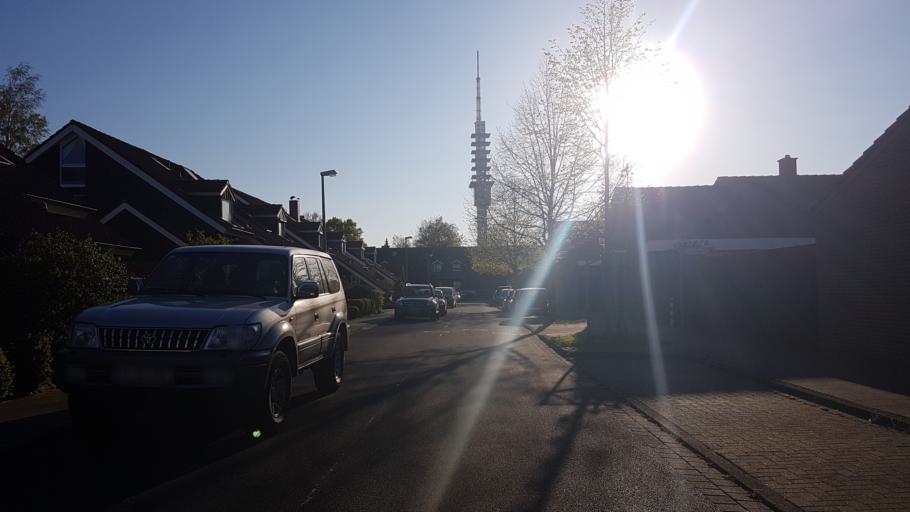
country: DE
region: Lower Saxony
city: Laatzen
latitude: 52.3943
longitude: 9.8117
